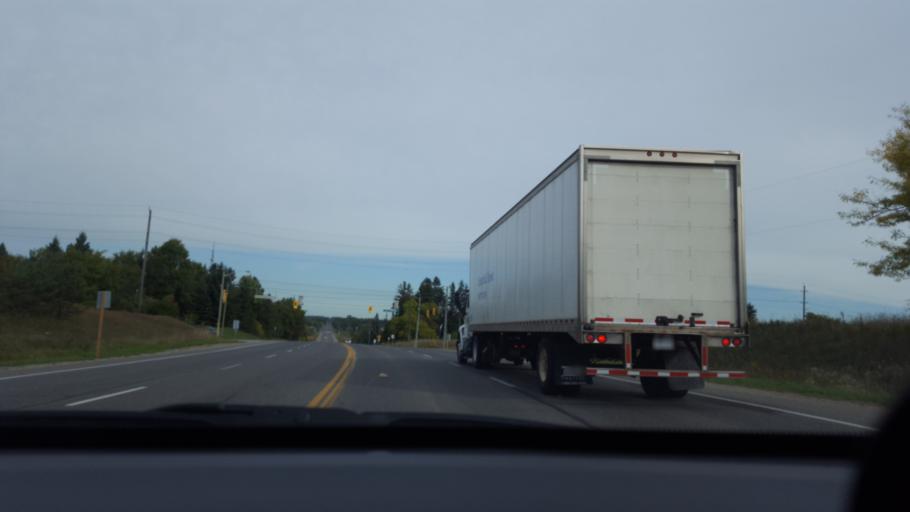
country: CA
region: Ontario
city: Vaughan
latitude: 43.9097
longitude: -79.5230
